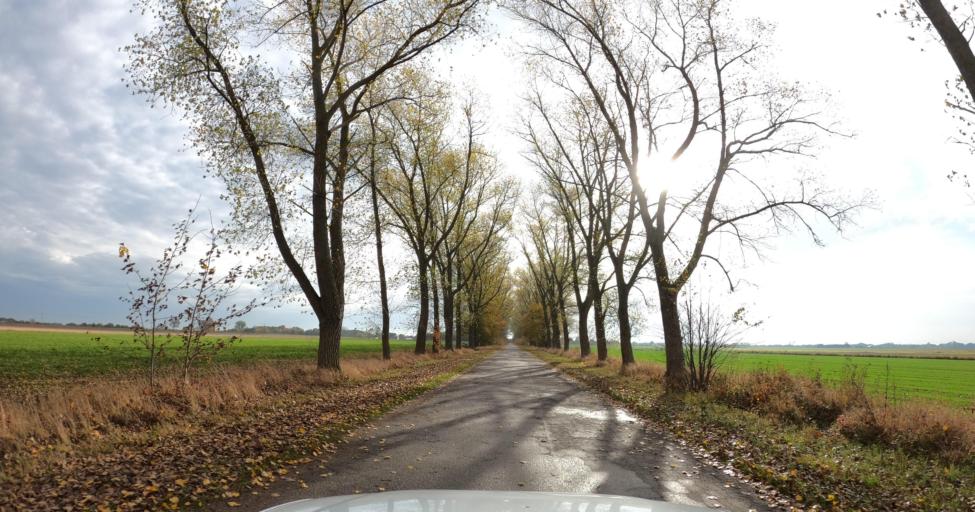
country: PL
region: West Pomeranian Voivodeship
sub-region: Powiat kamienski
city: Kamien Pomorski
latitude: 53.9979
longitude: 14.8379
